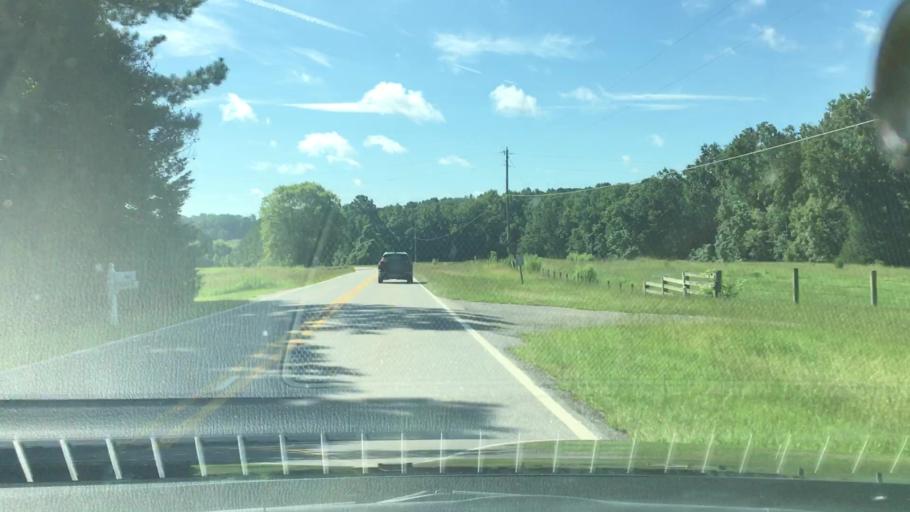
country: US
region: Georgia
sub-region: Putnam County
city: Jefferson
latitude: 33.3927
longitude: -83.2664
